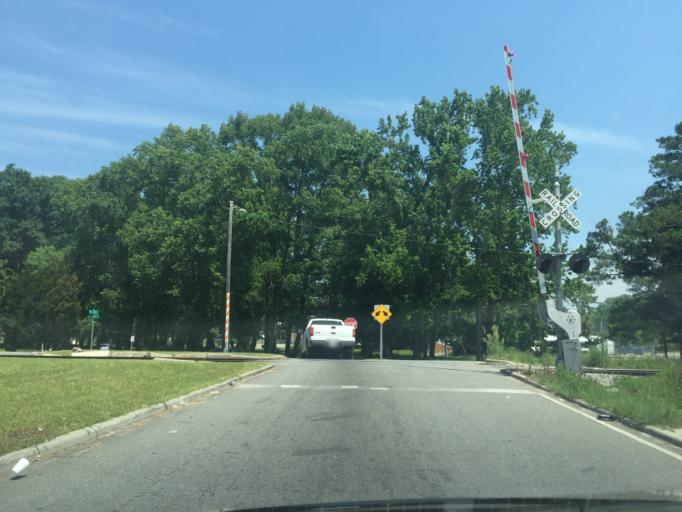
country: US
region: Georgia
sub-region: Chatham County
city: Savannah
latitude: 32.0476
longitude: -81.1107
